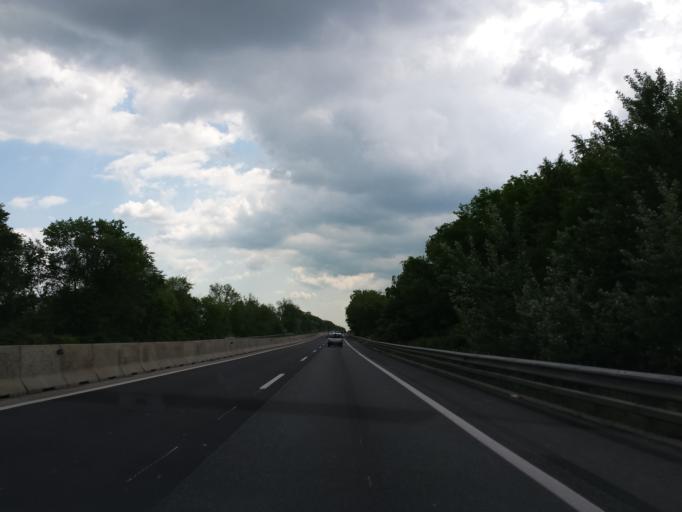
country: AT
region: Lower Austria
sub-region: Politischer Bezirk Bruck an der Leitha
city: Bruck an der Leitha
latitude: 48.0554
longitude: 16.7193
